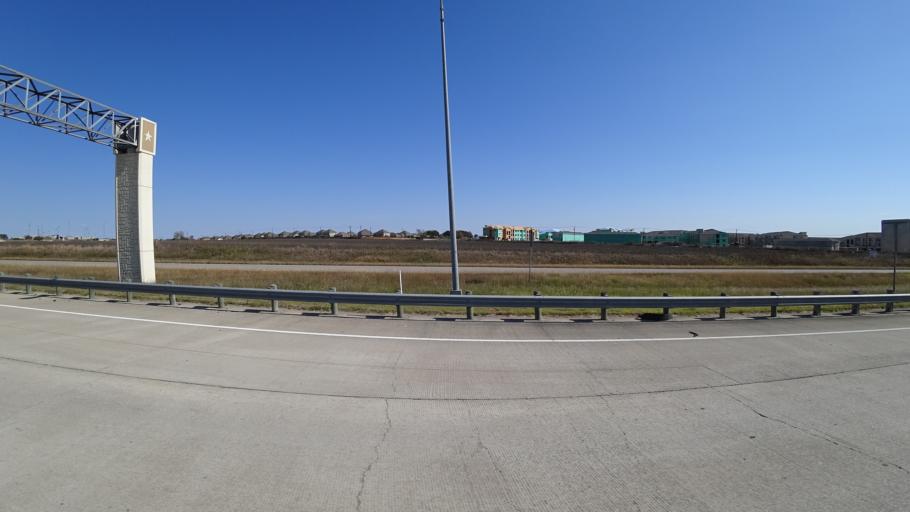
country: US
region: Texas
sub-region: Travis County
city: Pflugerville
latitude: 30.4574
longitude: -97.5940
